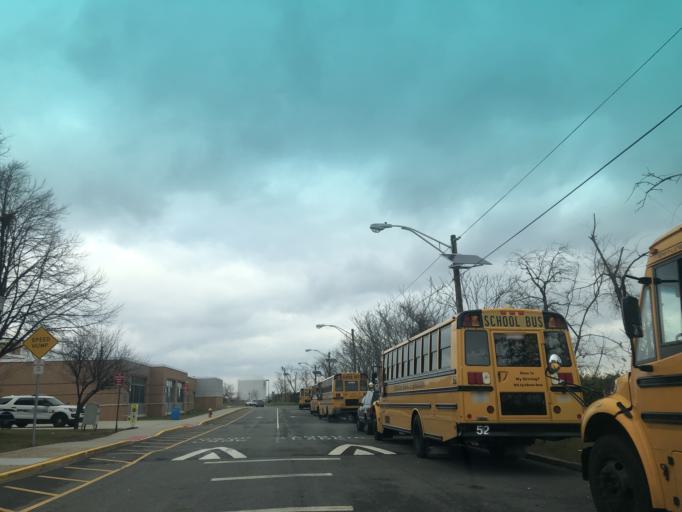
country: US
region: New Jersey
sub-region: Hudson County
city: Secaucus
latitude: 40.8036
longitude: -74.0503
